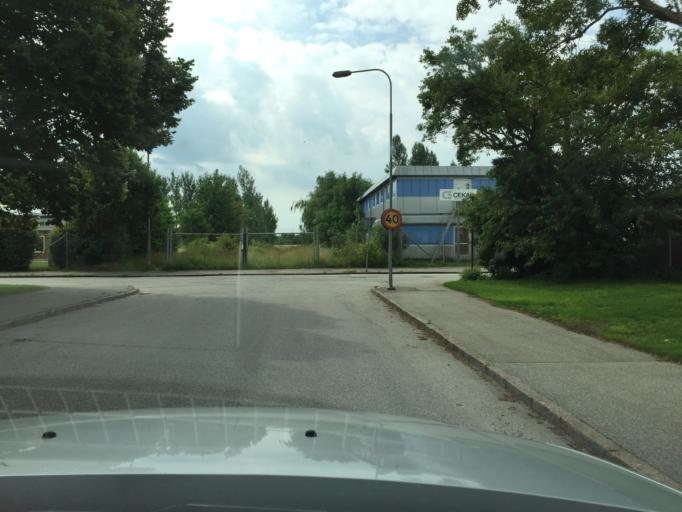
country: SE
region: Skane
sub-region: Lunds Kommun
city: Lund
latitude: 55.6992
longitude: 13.1651
